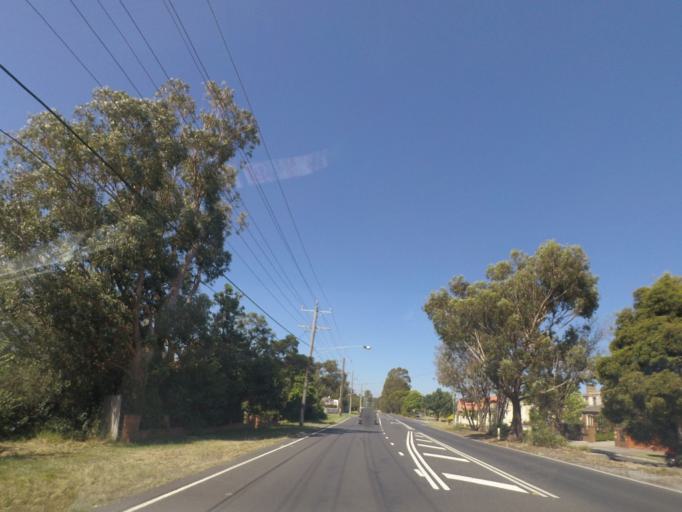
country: AU
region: Victoria
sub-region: Manningham
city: Bulleen
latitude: -37.7572
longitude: 145.0882
